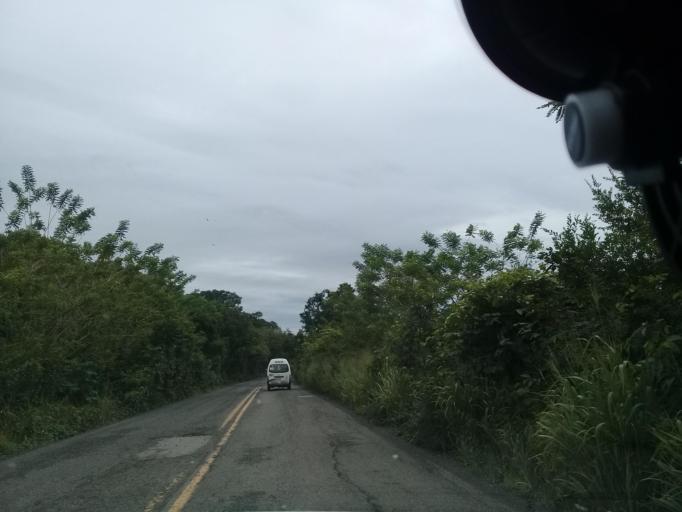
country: MX
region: Veracruz
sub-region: Chalma
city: San Pedro Coyutla
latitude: 21.2078
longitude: -98.3875
